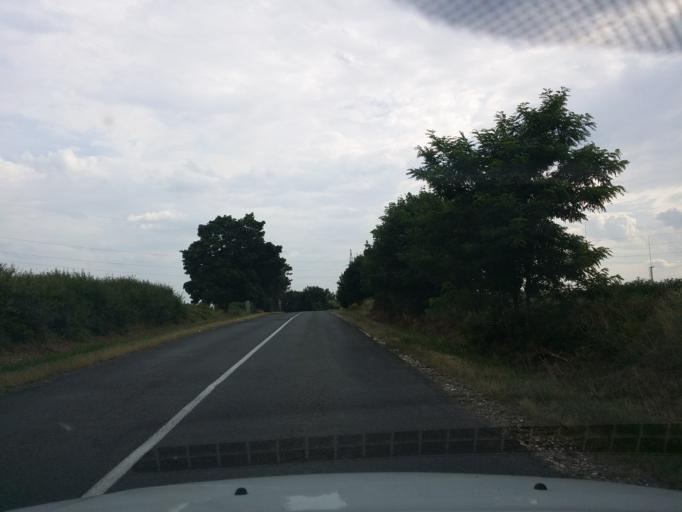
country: HU
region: Nograd
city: Bercel
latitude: 47.8913
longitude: 19.3693
